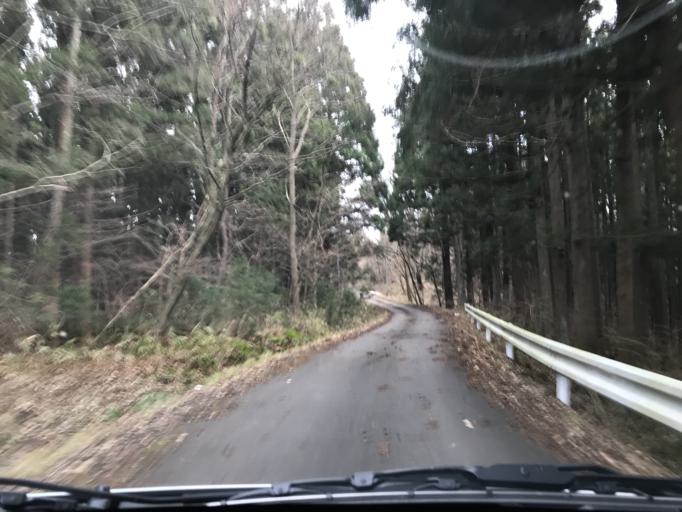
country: JP
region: Iwate
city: Ichinoseki
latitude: 38.9772
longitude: 141.0399
